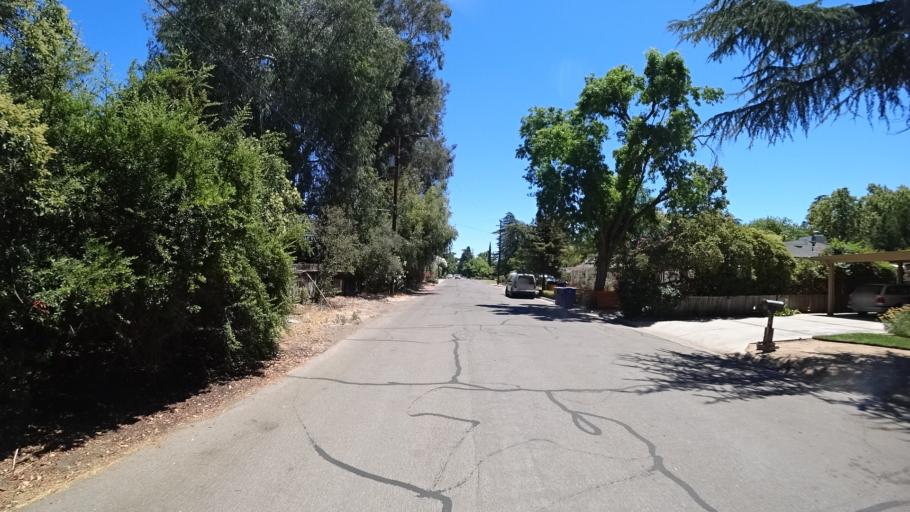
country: US
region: California
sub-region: Fresno County
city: Fresno
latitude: 36.7849
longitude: -119.8055
